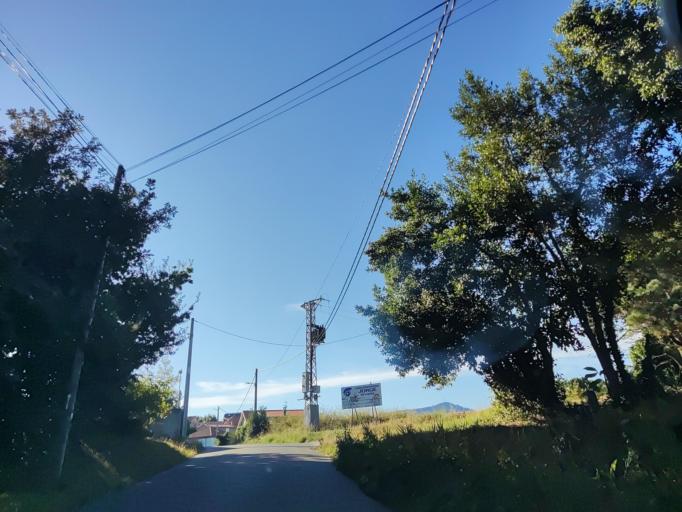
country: ES
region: Galicia
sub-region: Provincia da Coruna
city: Boiro
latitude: 42.5905
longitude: -8.9258
